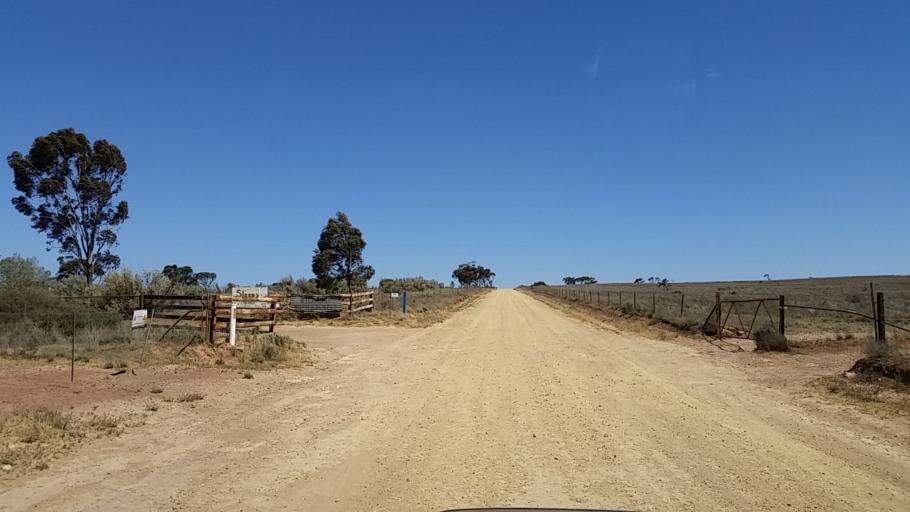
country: AU
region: South Australia
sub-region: Peterborough
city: Peterborough
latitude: -32.9843
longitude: 138.8318
